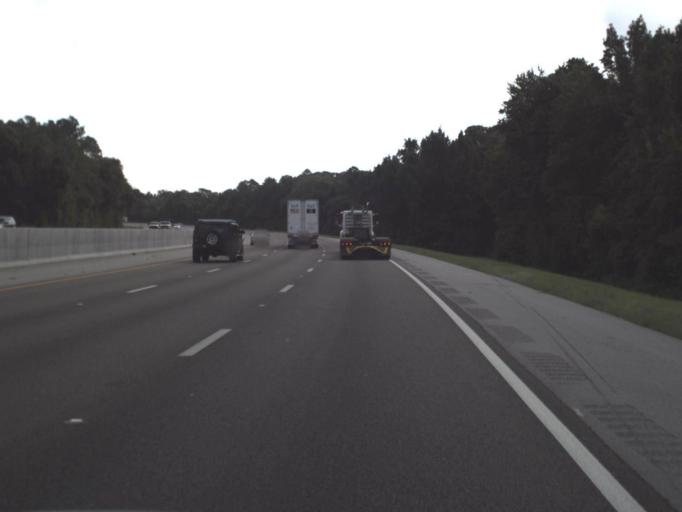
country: US
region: Florida
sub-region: Hillsborough County
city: University
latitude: 28.1084
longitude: -82.4286
